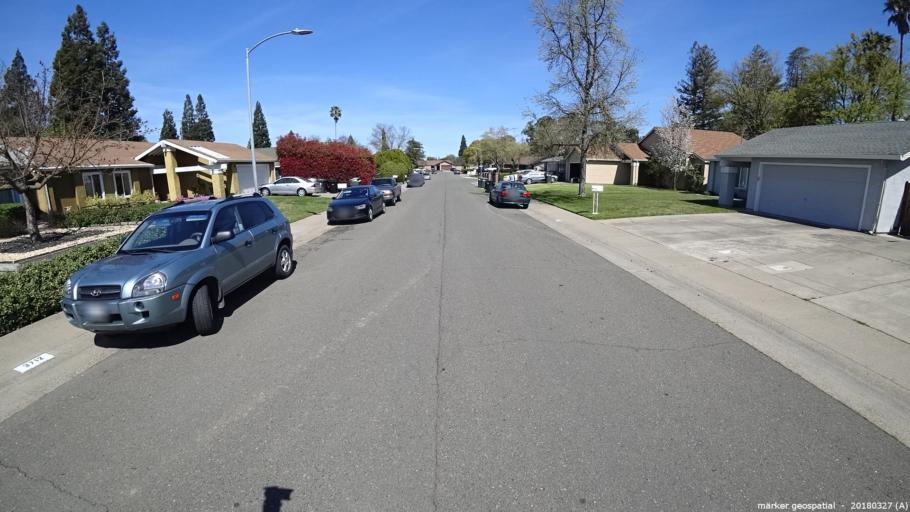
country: US
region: California
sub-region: Sacramento County
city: La Riviera
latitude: 38.5523
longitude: -121.3435
